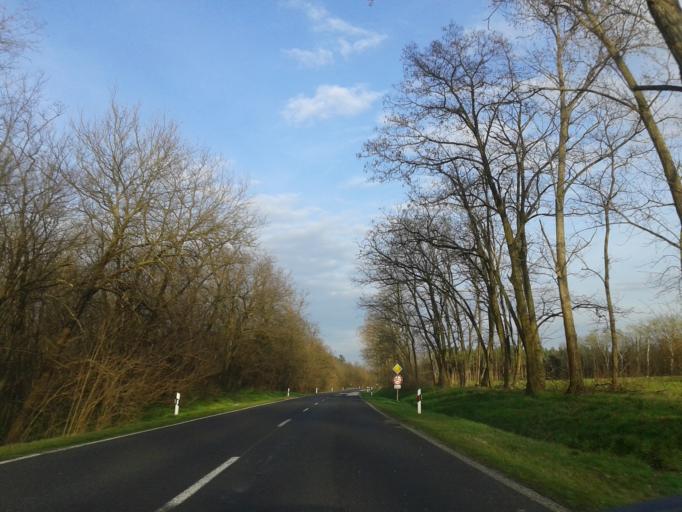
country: HU
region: Komarom-Esztergom
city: Acs
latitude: 47.7391
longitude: 17.9360
